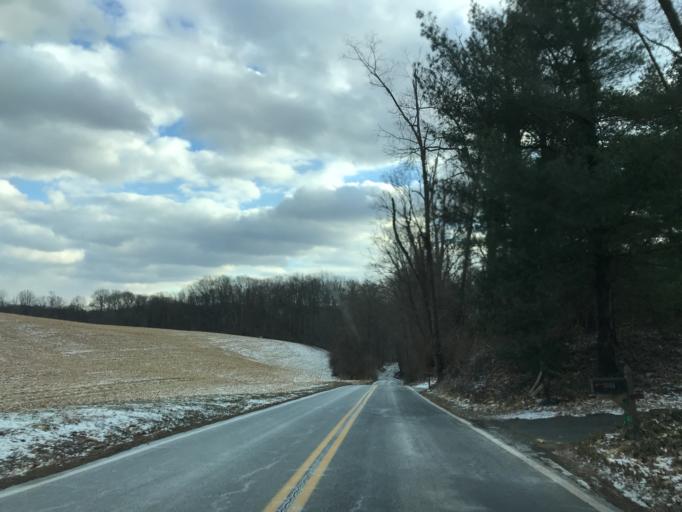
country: US
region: Maryland
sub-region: Harford County
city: Bel Air North
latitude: 39.6359
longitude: -76.3764
